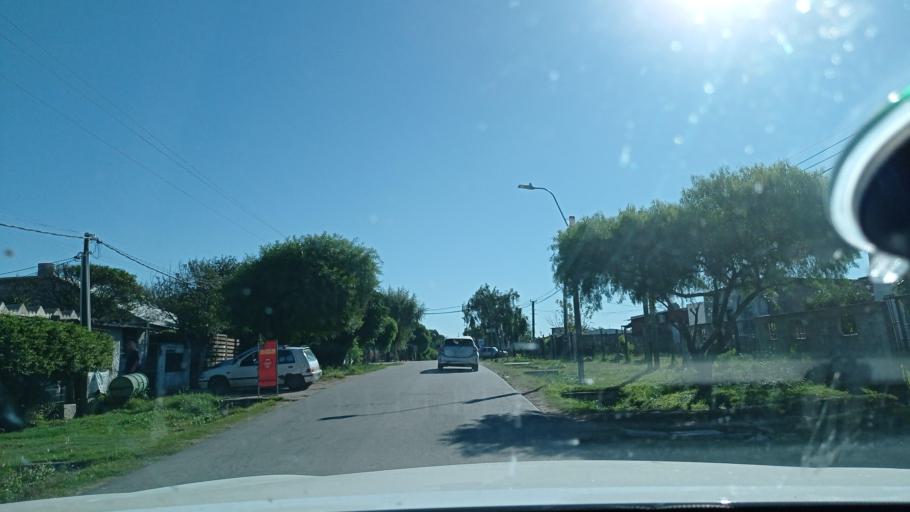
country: UY
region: Canelones
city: Joaquin Suarez
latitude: -34.7561
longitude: -55.9917
